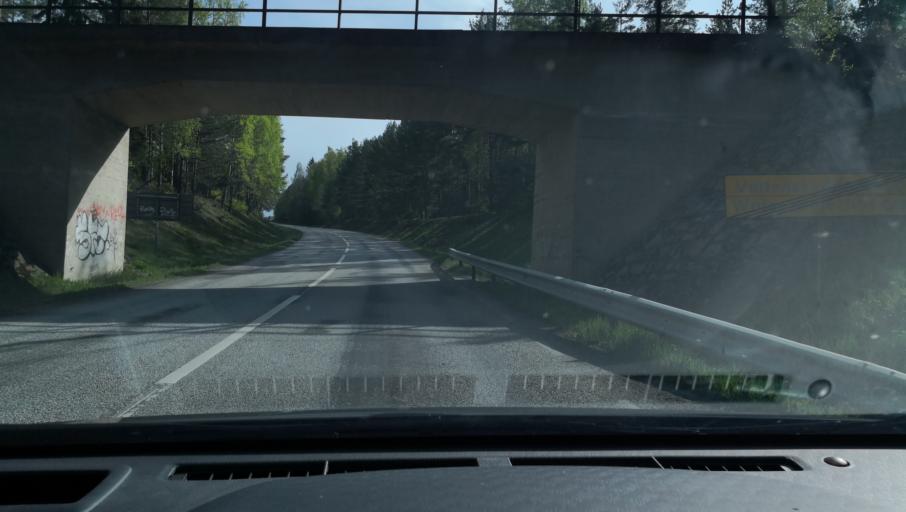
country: SE
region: OErebro
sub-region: Askersunds Kommun
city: Asbro
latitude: 59.0439
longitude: 15.0399
